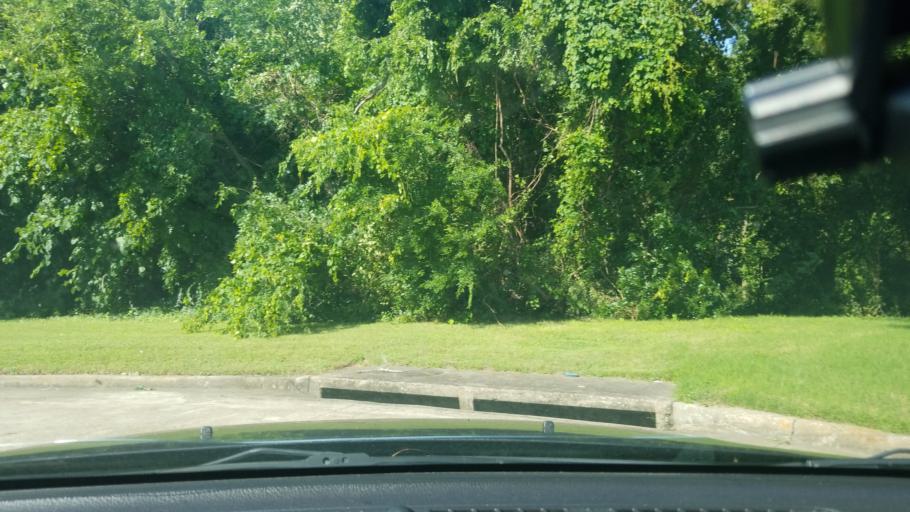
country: US
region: Texas
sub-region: Dallas County
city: Mesquite
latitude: 32.7746
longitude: -96.5756
